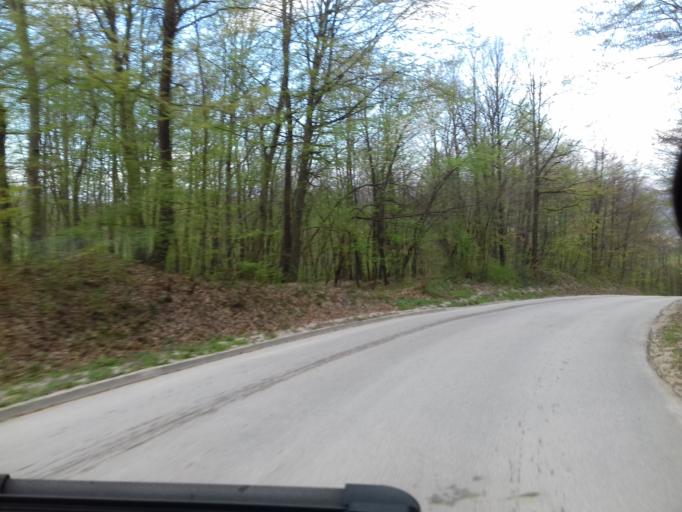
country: BA
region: Federation of Bosnia and Herzegovina
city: Tesanjka
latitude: 44.6497
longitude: 18.0367
